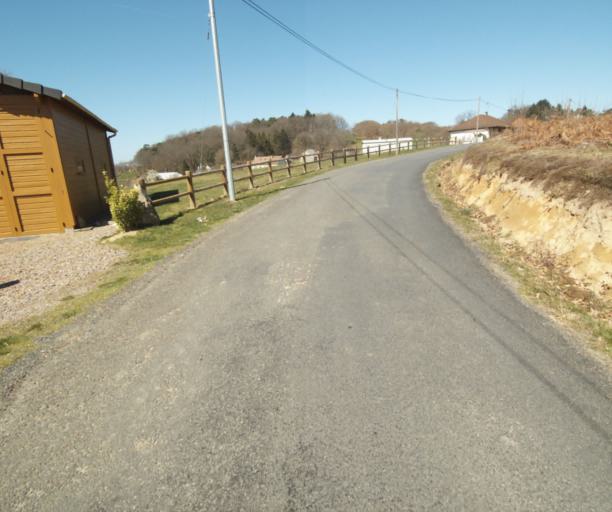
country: FR
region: Limousin
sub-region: Departement de la Correze
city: Saint-Mexant
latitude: 45.2860
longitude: 1.6414
